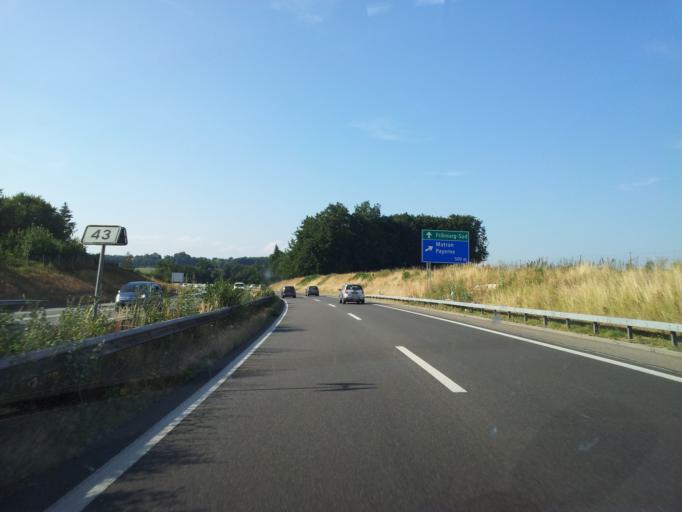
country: CH
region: Fribourg
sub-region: Sarine District
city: Matran
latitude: 46.7737
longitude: 7.0937
